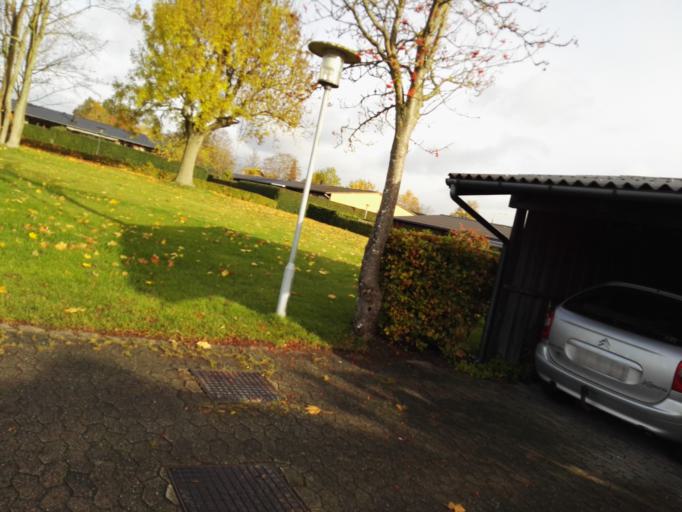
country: DK
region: Capital Region
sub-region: Ballerup Kommune
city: Ballerup
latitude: 55.7100
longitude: 12.3934
